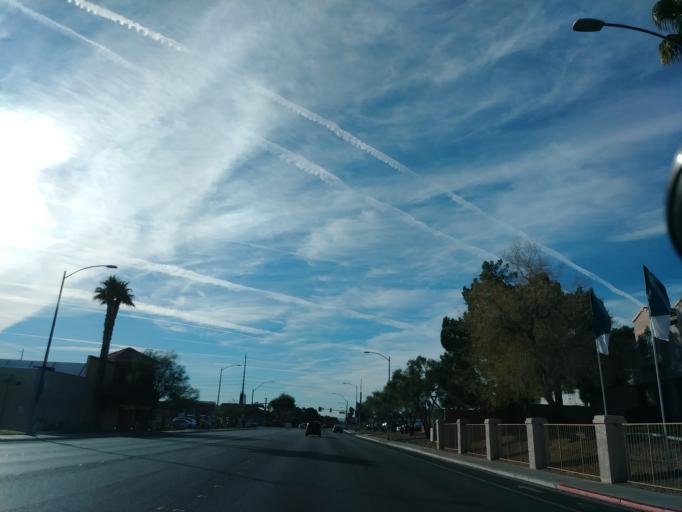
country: US
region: Nevada
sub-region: Clark County
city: Spring Valley
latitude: 36.1456
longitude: -115.2340
